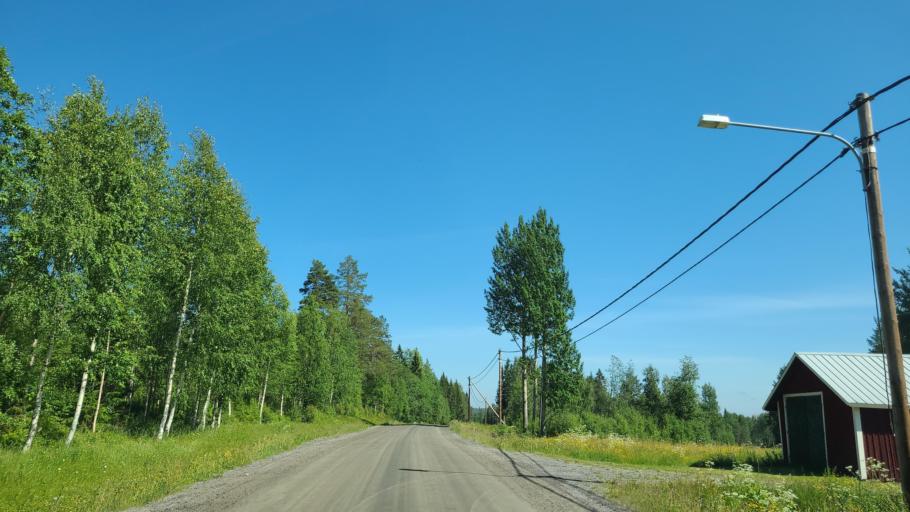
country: SE
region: Vaesterbotten
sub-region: Bjurholms Kommun
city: Bjurholm
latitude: 63.6396
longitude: 19.1870
